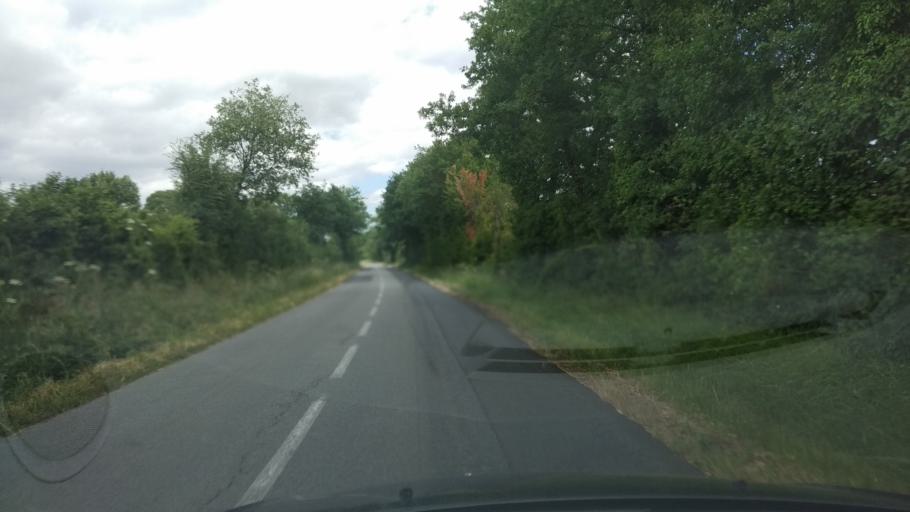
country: FR
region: Poitou-Charentes
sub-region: Departement de la Vienne
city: Vouneuil-sous-Biard
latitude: 46.5643
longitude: 0.2677
